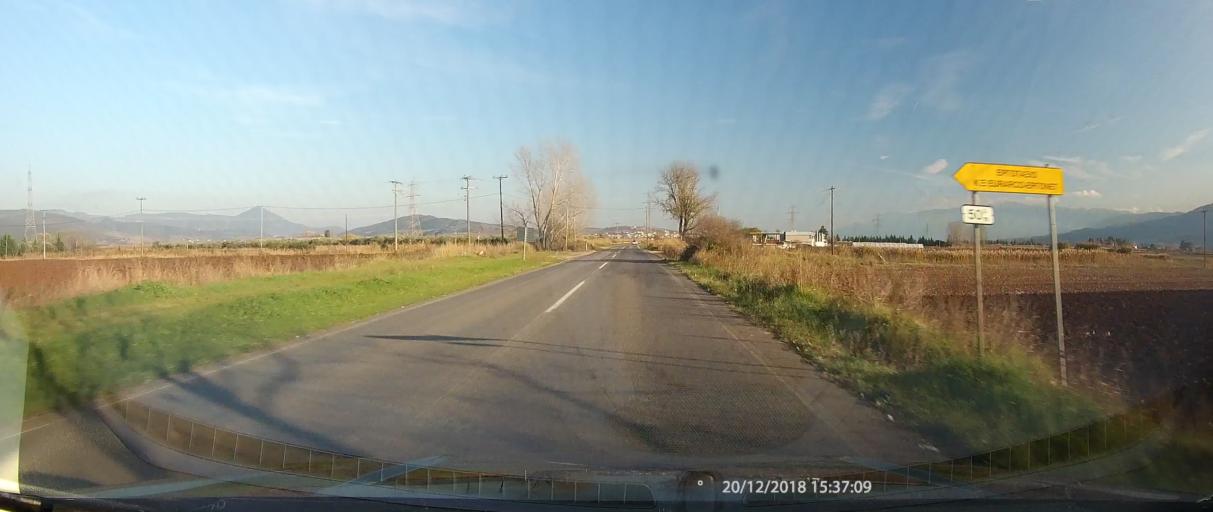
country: GR
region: Central Greece
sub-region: Nomos Fthiotidos
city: Lianokladhion
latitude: 38.9134
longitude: 22.3239
